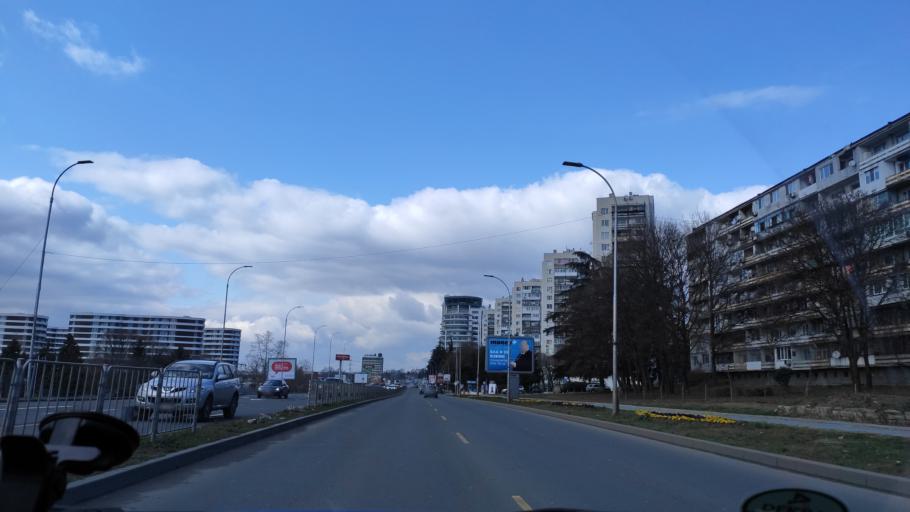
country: BG
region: Varna
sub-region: Obshtina Varna
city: Varna
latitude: 43.2206
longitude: 27.8827
